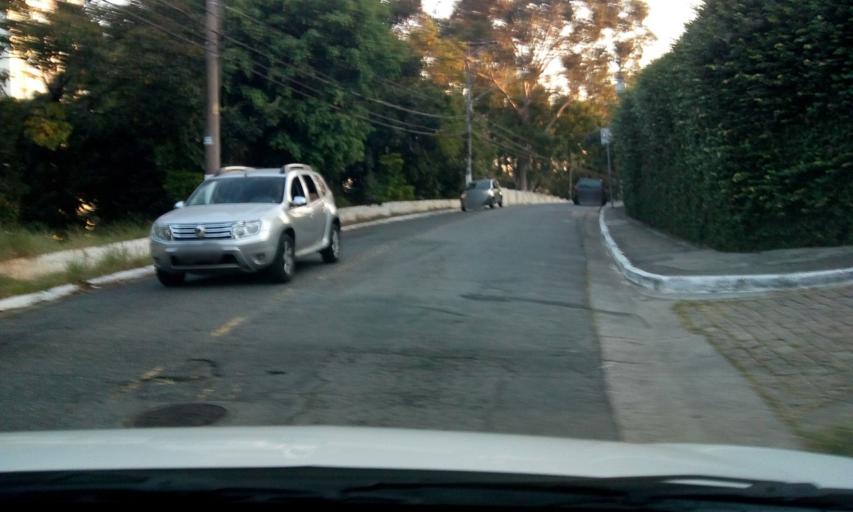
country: BR
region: Sao Paulo
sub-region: Sao Paulo
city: Sao Paulo
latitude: -23.4936
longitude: -46.6121
